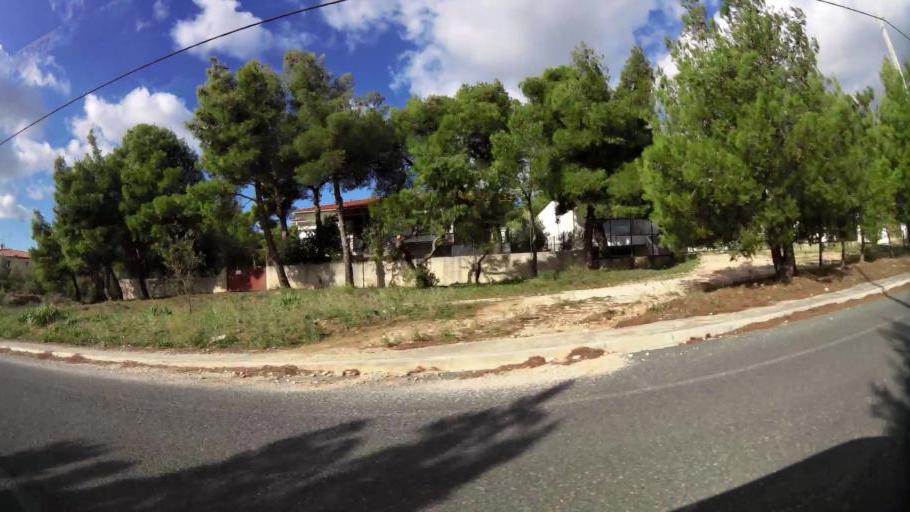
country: GR
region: Attica
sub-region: Nomarchia Anatolikis Attikis
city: Thrakomakedones
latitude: 38.1283
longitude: 23.7679
